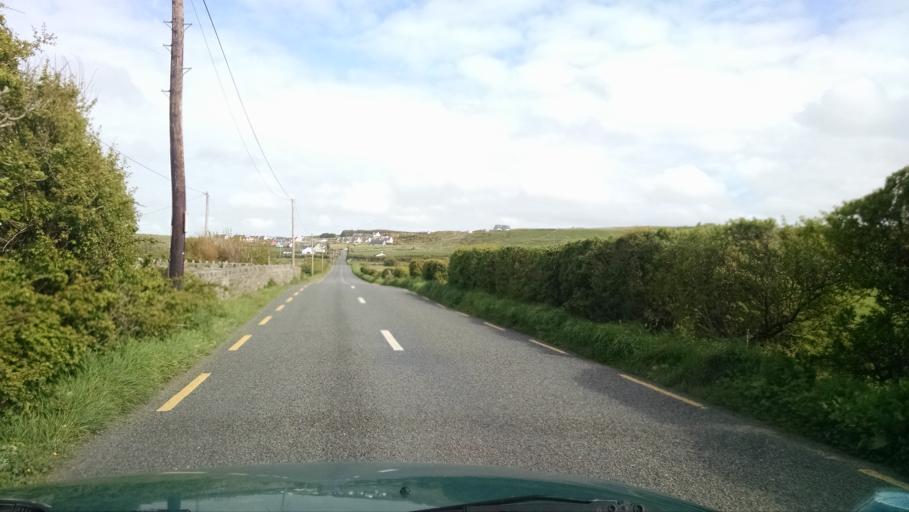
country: IE
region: Connaught
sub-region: County Galway
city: Bearna
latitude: 53.0124
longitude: -9.3691
